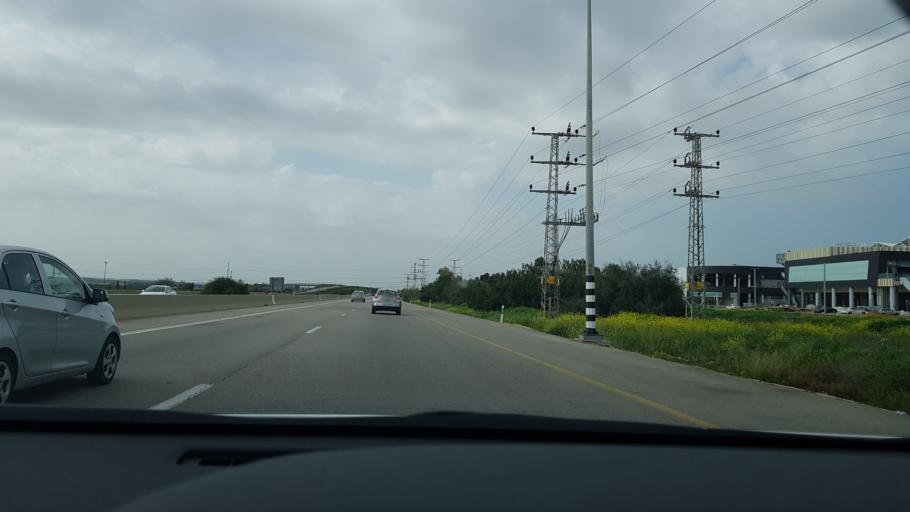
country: IL
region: Southern District
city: Ashqelon
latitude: 31.6265
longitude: 34.5849
